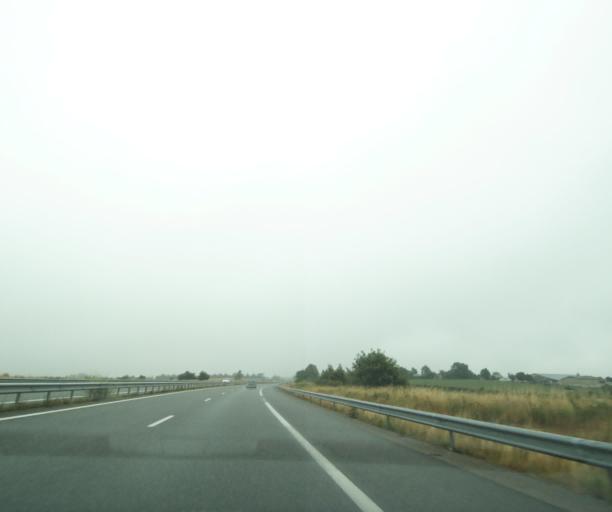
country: FR
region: Midi-Pyrenees
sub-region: Departement de l'Aveyron
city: Naucelle
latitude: 44.1306
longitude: 2.3081
